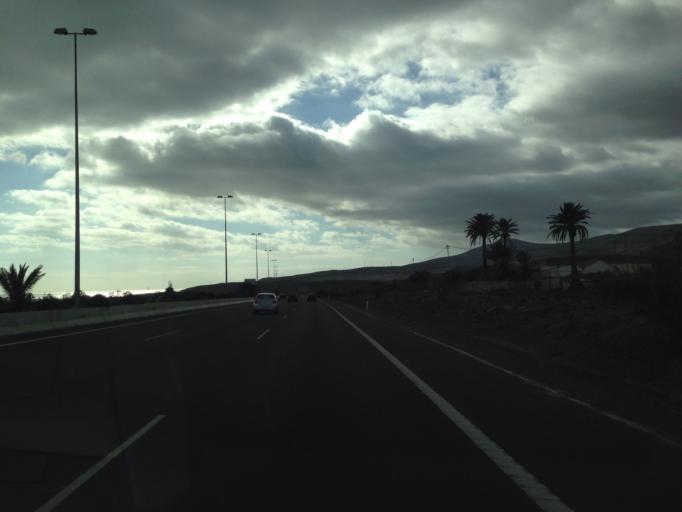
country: ES
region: Canary Islands
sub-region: Provincia de Las Palmas
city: Cruce de Arinaga
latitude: 27.8210
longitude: -15.4640
